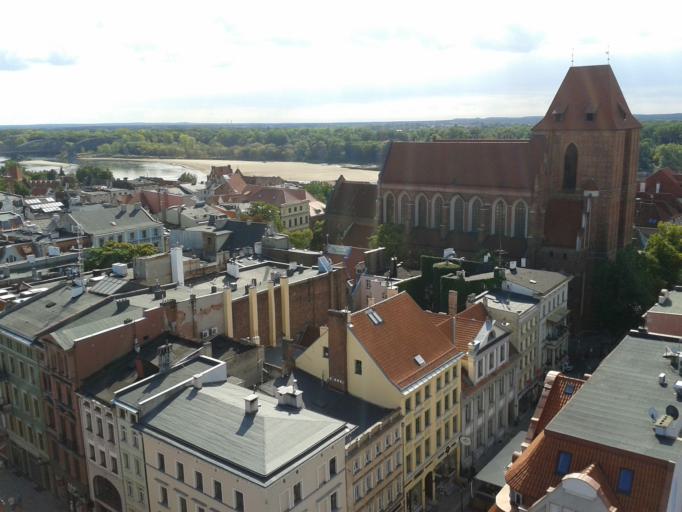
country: PL
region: Kujawsko-Pomorskie
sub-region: Torun
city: Torun
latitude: 53.0104
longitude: 18.6047
